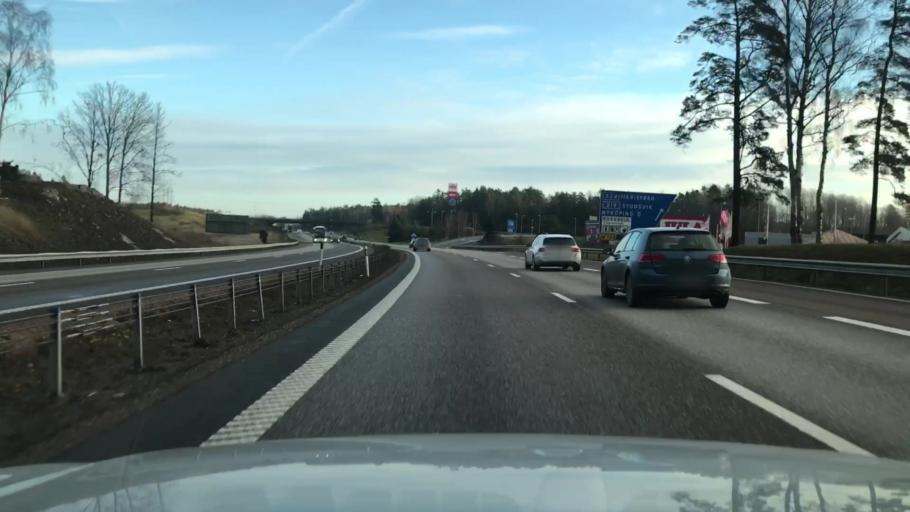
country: SE
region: Soedermanland
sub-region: Nykopings Kommun
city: Nykoping
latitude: 58.7714
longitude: 17.0191
